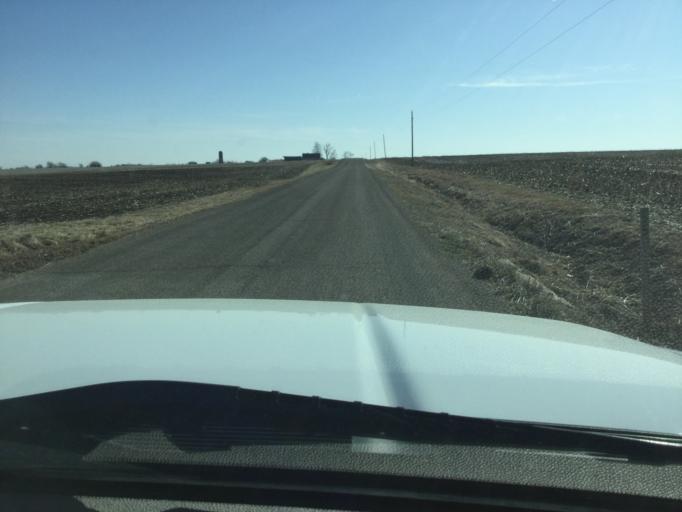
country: US
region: Kansas
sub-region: Brown County
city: Horton
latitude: 39.7254
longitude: -95.4638
